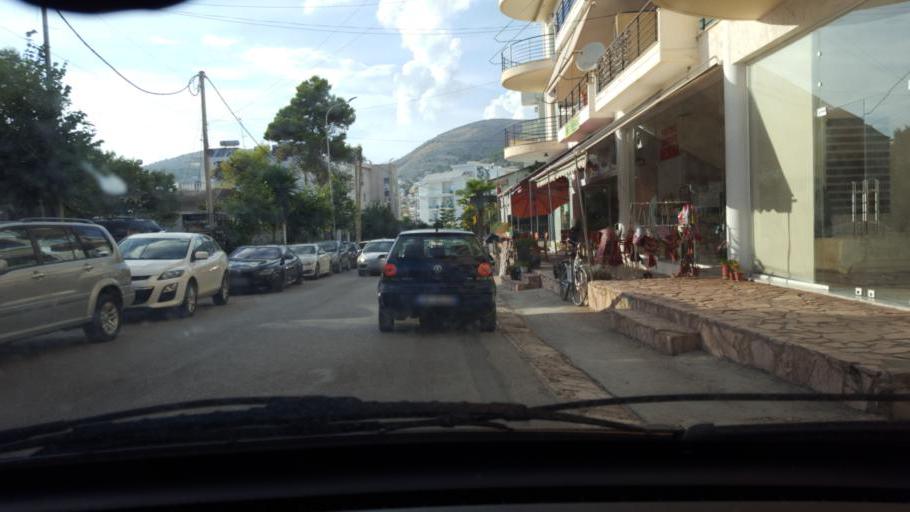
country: AL
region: Vlore
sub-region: Rrethi i Sarandes
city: Sarande
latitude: 39.8683
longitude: 20.0150
